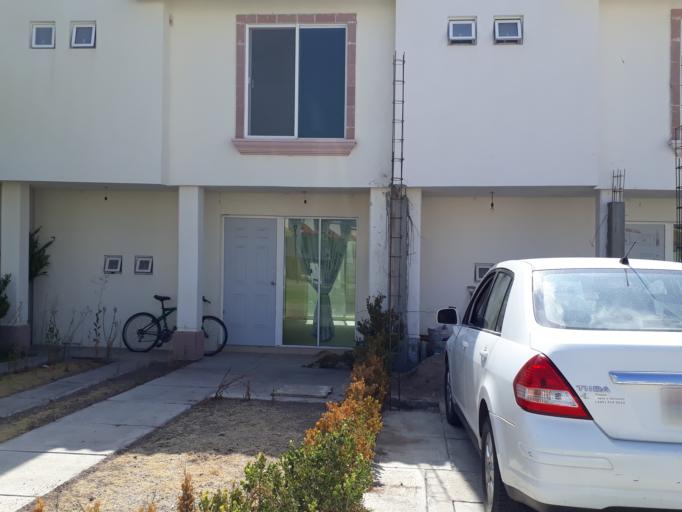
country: MX
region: Aguascalientes
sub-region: Aguascalientes
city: San Sebastian [Fraccionamiento]
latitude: 21.8072
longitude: -102.2925
